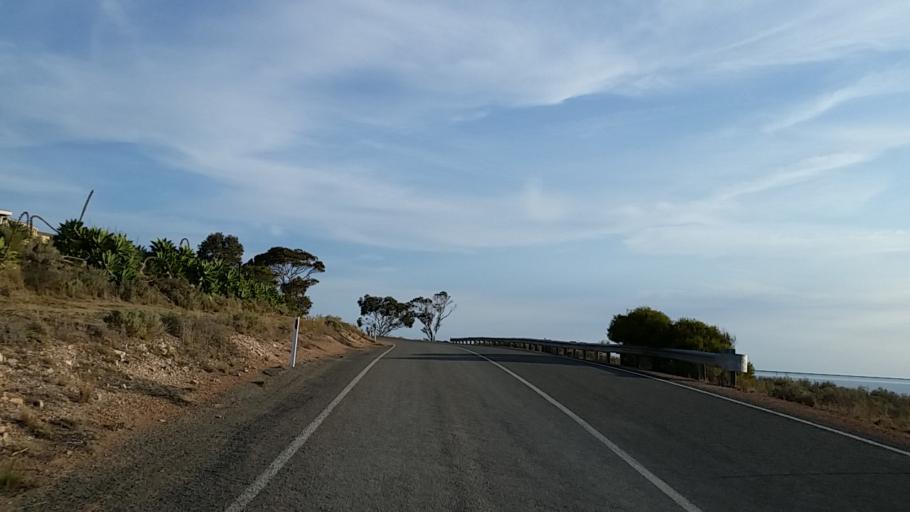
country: AU
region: South Australia
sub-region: Port Pirie City and Dists
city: Port Pirie
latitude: -33.1026
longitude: 138.0251
